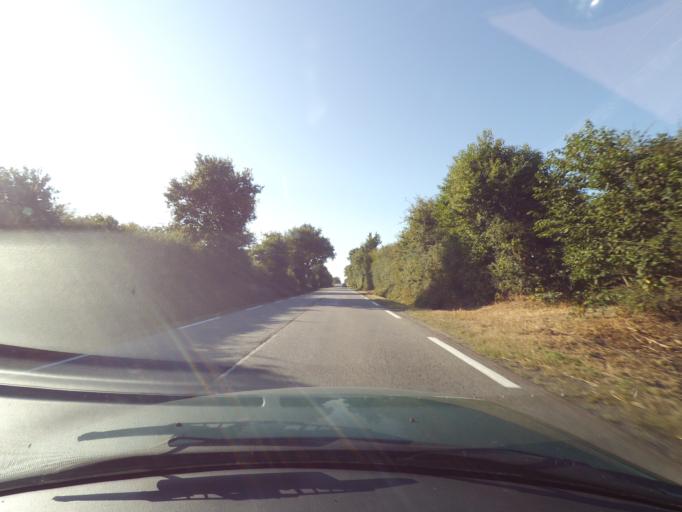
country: FR
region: Poitou-Charentes
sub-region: Departement des Deux-Sevres
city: Viennay
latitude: 46.6934
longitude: -0.2747
